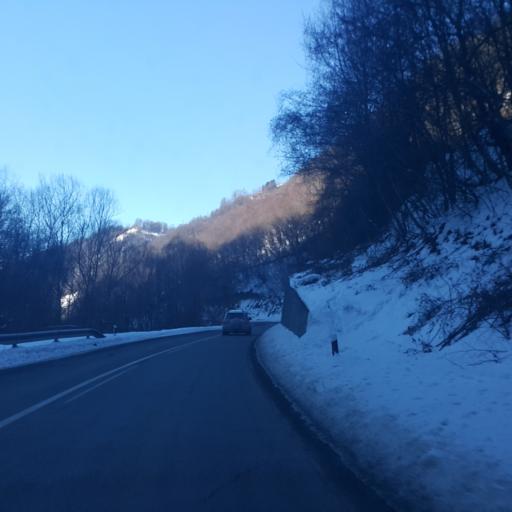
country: RS
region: Central Serbia
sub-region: Rasinski Okrug
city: Aleksandrovac
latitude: 43.3265
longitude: 20.9259
